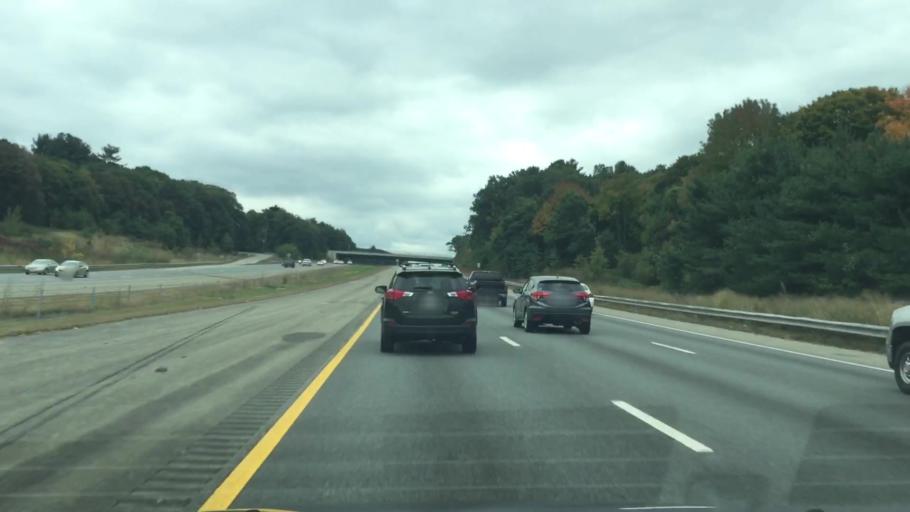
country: US
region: Massachusetts
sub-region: Middlesex County
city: Billerica
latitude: 42.5473
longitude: -71.2872
